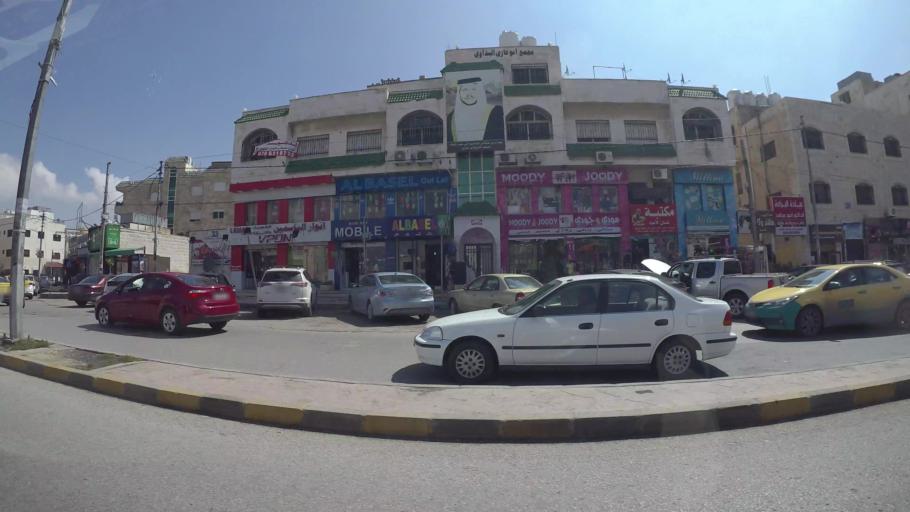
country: JO
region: Amman
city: Al Bunayyat ash Shamaliyah
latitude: 31.9179
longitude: 35.8923
